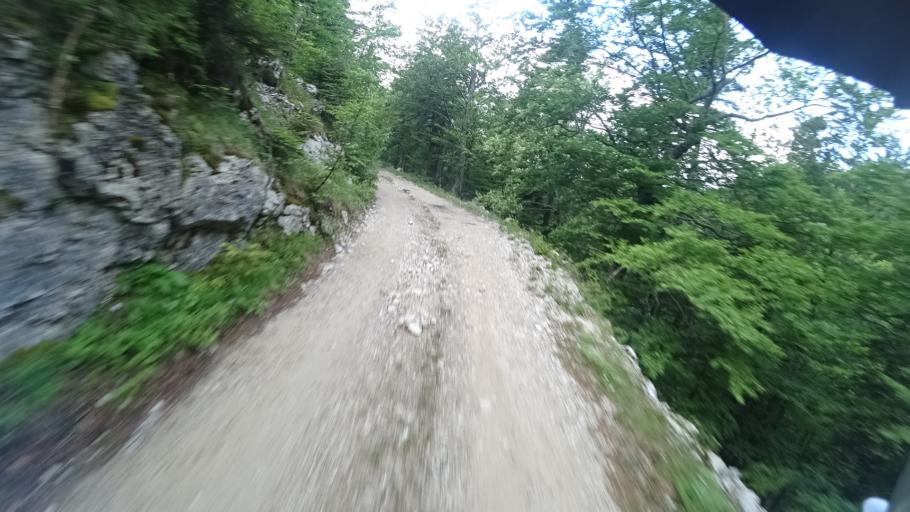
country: BA
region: Federation of Bosnia and Herzegovina
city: Izacic
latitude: 44.7573
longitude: 15.7637
